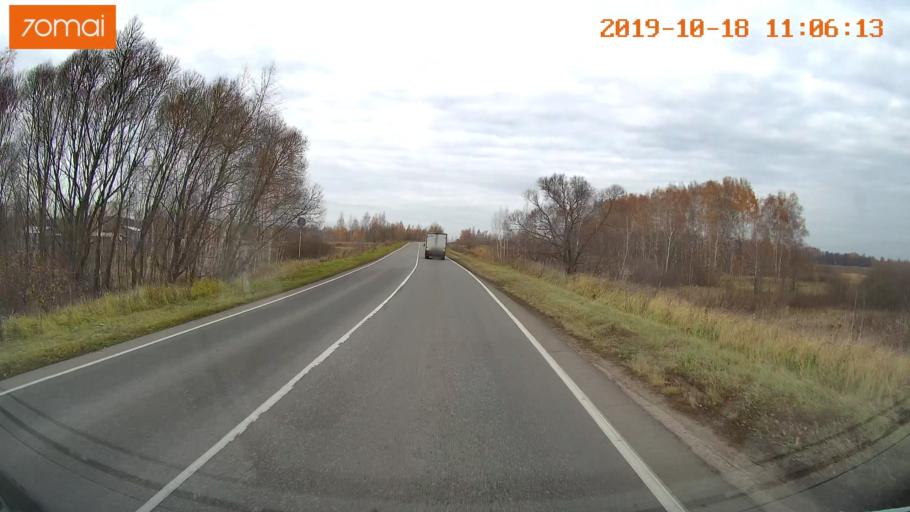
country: RU
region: Tula
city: Kimovsk
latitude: 53.9173
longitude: 38.5406
